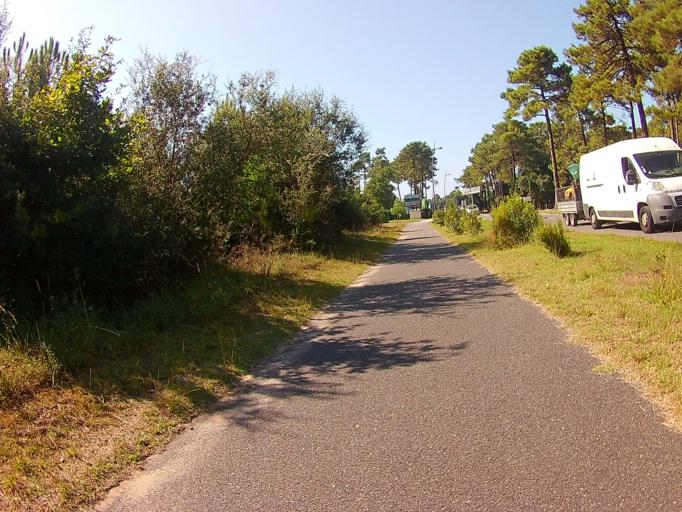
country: FR
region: Aquitaine
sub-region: Departement des Landes
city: Labenne
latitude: 43.5942
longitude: -1.4540
